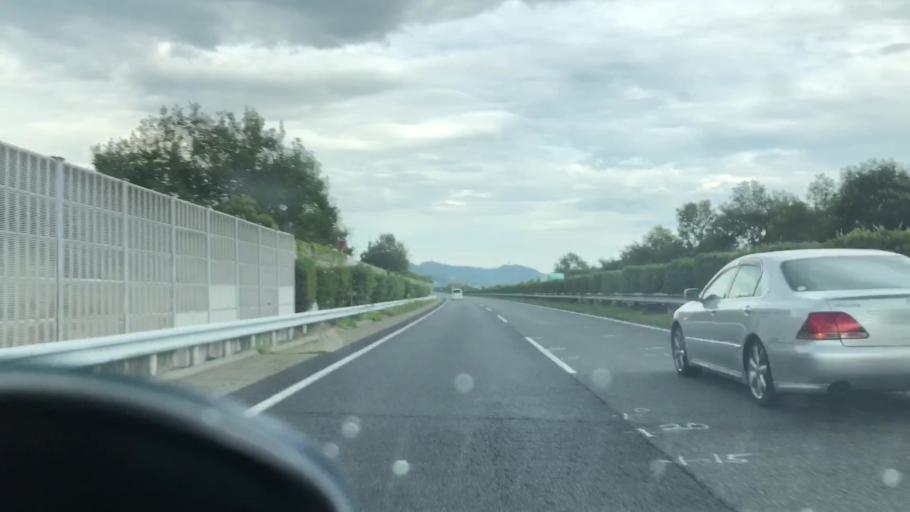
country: JP
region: Hyogo
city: Ono
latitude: 34.9425
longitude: 134.8140
